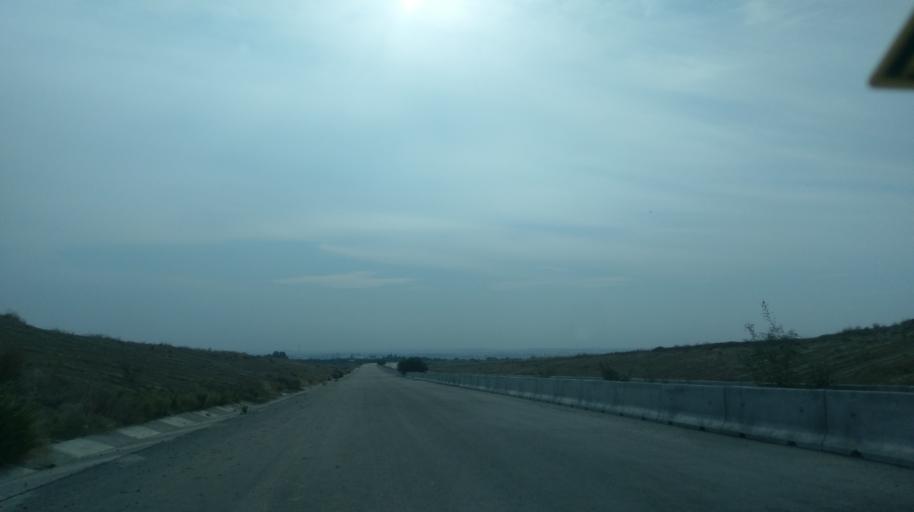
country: CY
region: Lefkosia
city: Nicosia
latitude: 35.2230
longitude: 33.4009
